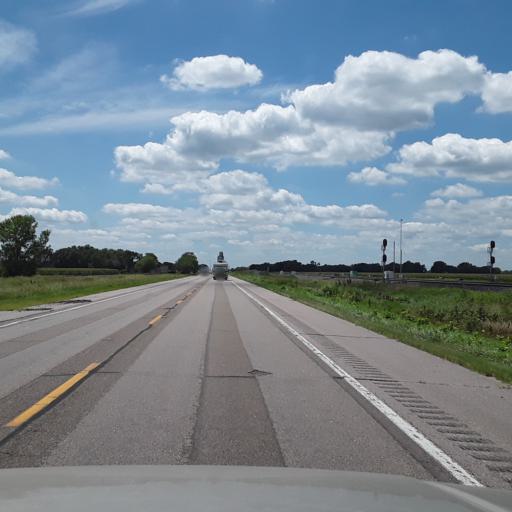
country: US
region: Nebraska
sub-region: Nance County
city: Genoa
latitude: 41.3220
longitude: -97.6490
